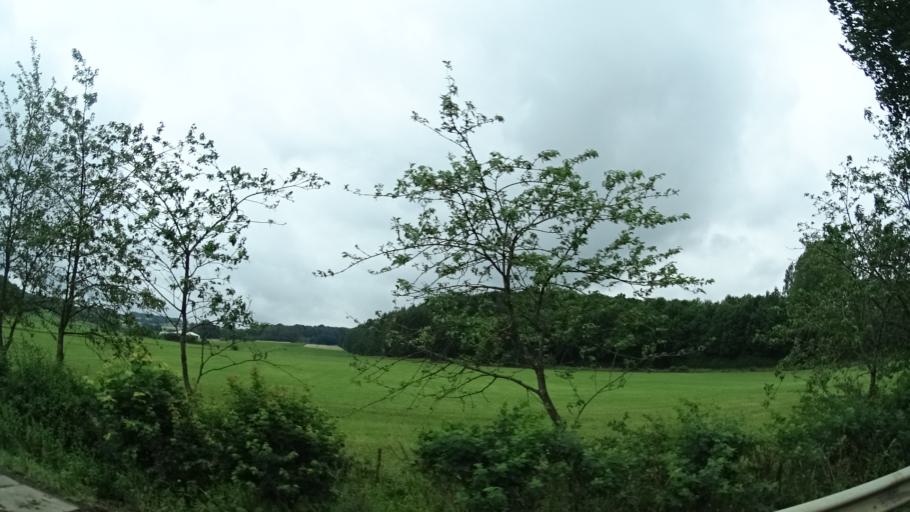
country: LU
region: Luxembourg
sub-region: Canton de Capellen
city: Garnich
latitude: 49.6331
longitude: 5.9560
